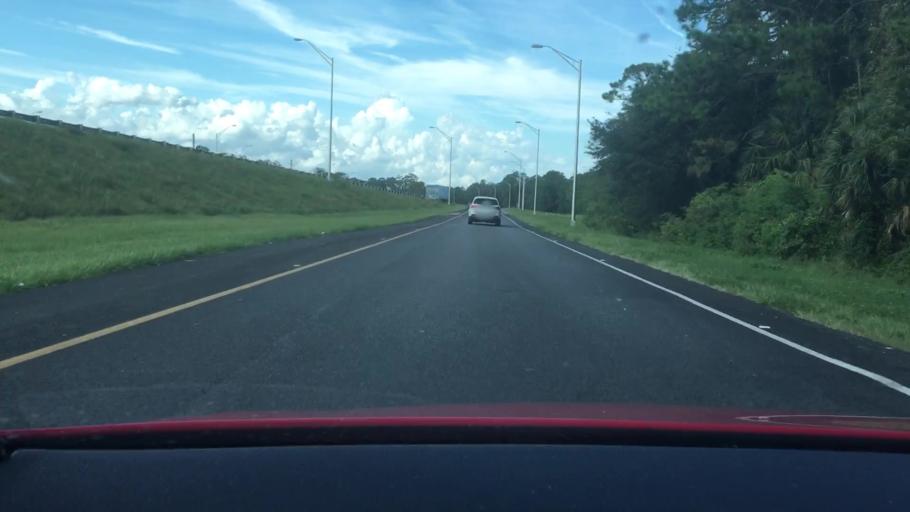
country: US
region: Florida
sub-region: Volusia County
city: Port Orange
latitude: 29.1087
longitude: -81.0295
